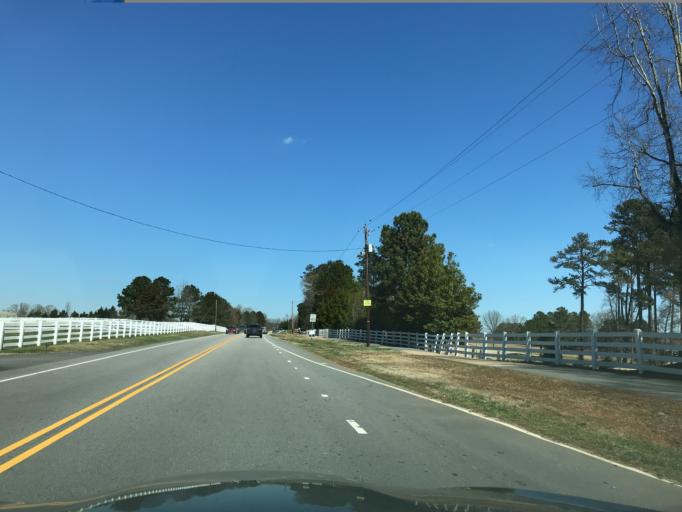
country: US
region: North Carolina
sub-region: Wake County
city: Wake Forest
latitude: 35.9558
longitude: -78.5661
